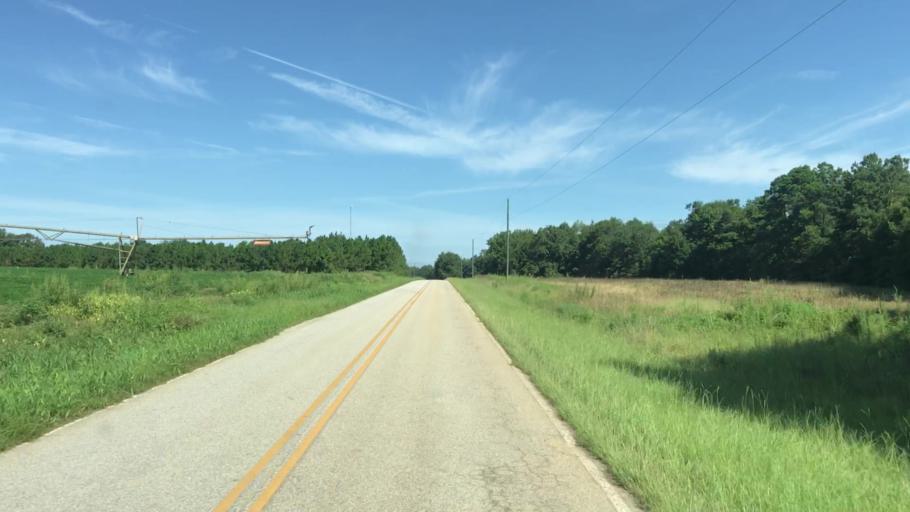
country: US
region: Georgia
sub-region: Jefferson County
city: Wadley
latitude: 32.8400
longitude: -82.3928
